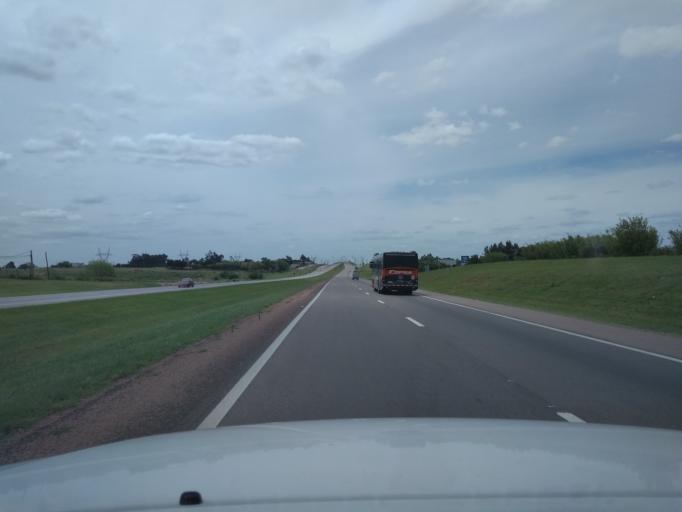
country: UY
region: Canelones
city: Las Piedras
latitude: -34.7308
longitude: -56.2487
